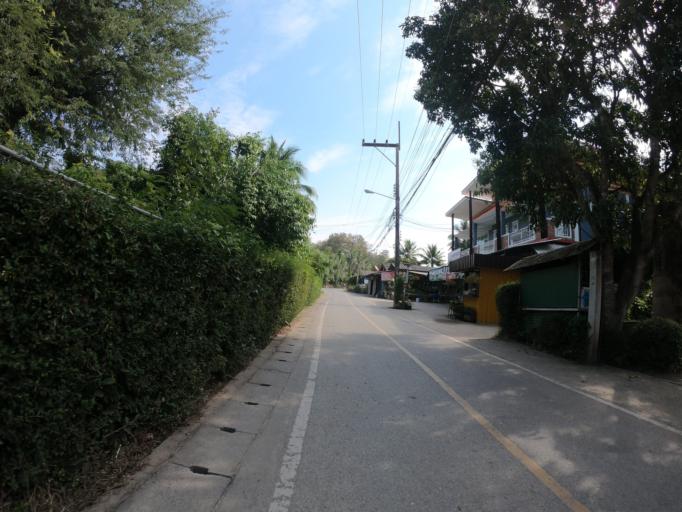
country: TH
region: Chiang Mai
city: San Sai
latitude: 18.8614
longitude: 99.0604
